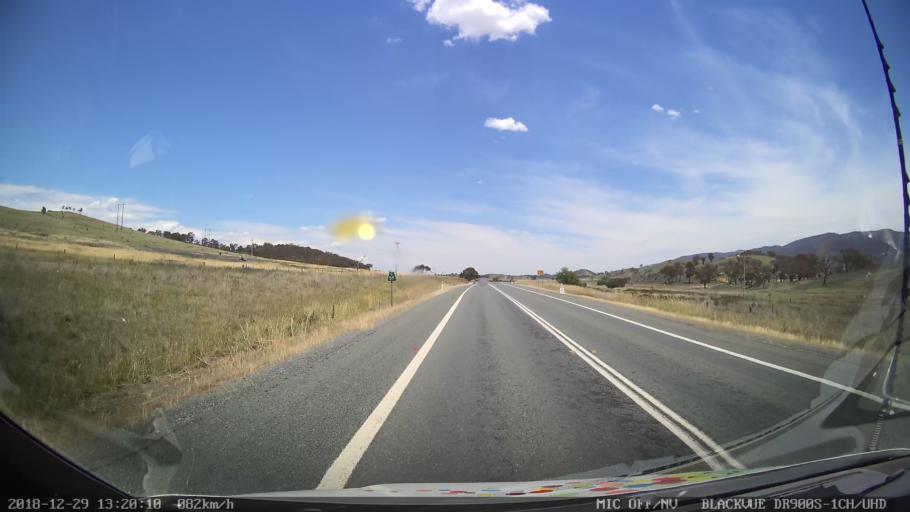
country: AU
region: Australian Capital Territory
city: Macarthur
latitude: -35.7754
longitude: 149.1620
